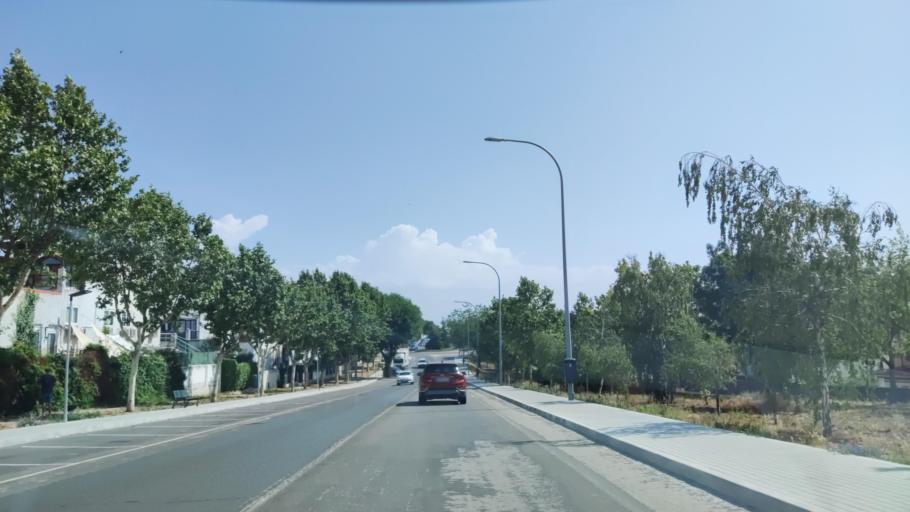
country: ES
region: Madrid
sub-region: Provincia de Madrid
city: Navalcarnero
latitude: 40.2839
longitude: -4.0225
